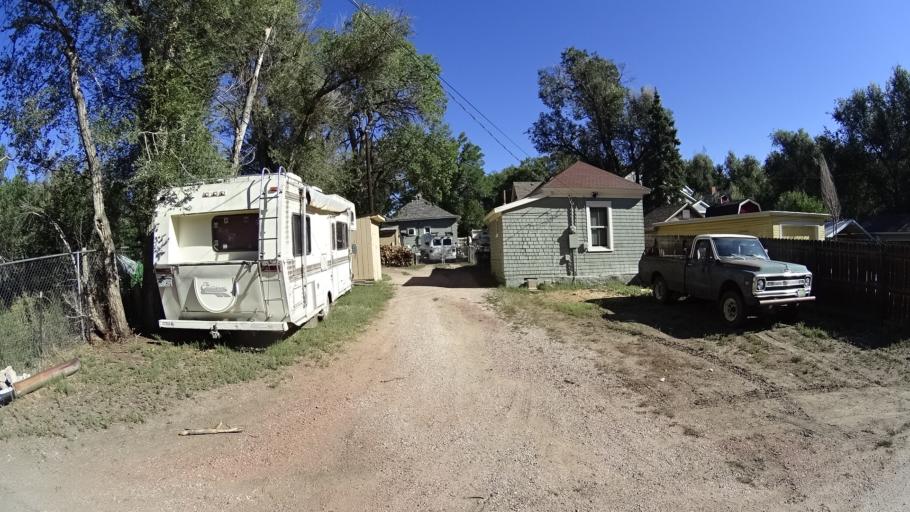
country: US
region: Colorado
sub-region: El Paso County
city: Colorado Springs
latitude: 38.8413
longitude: -104.8136
